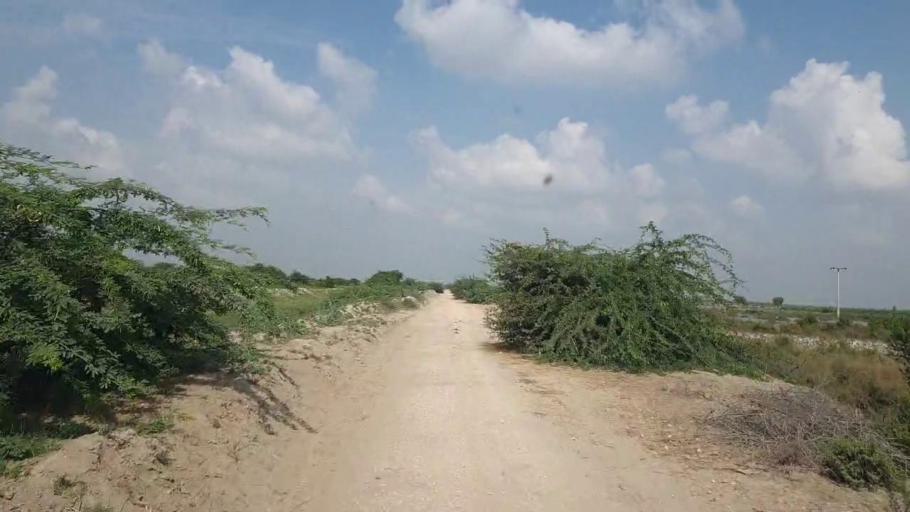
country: PK
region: Sindh
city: Badin
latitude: 24.5019
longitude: 68.6557
